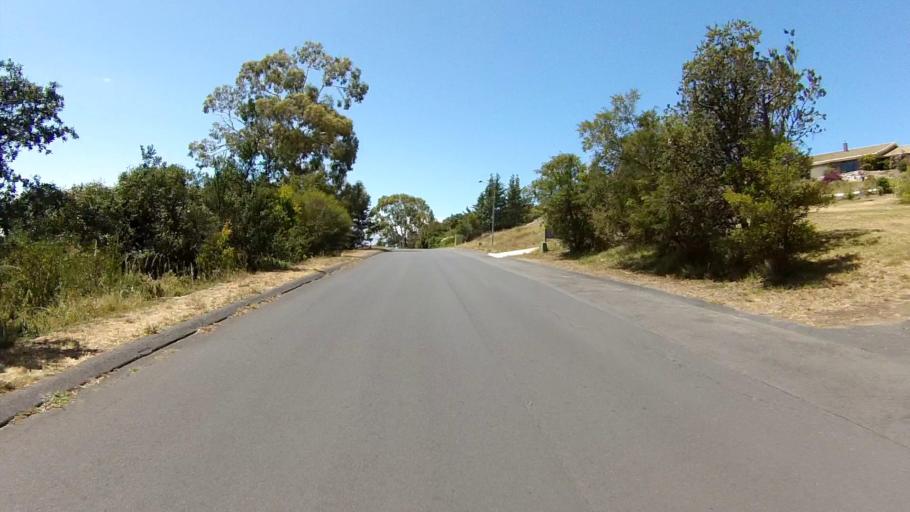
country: AU
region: Tasmania
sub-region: Clarence
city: Sandford
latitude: -42.9193
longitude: 147.5055
